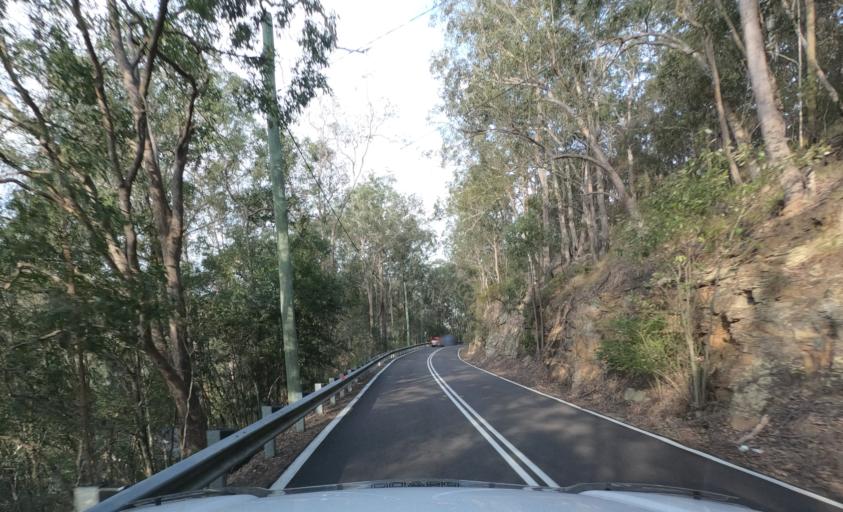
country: AU
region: New South Wales
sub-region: Wyong Shire
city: Little Jilliby
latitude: -33.2246
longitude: 151.2744
